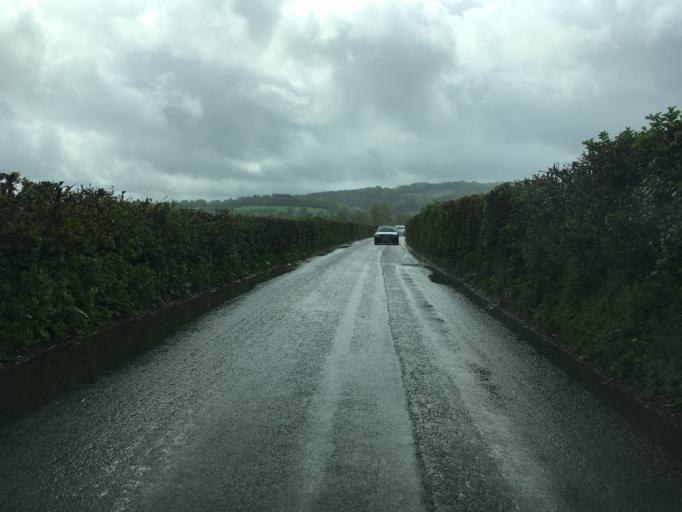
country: GB
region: England
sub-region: North Somerset
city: Burrington
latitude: 51.3403
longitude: -2.7465
